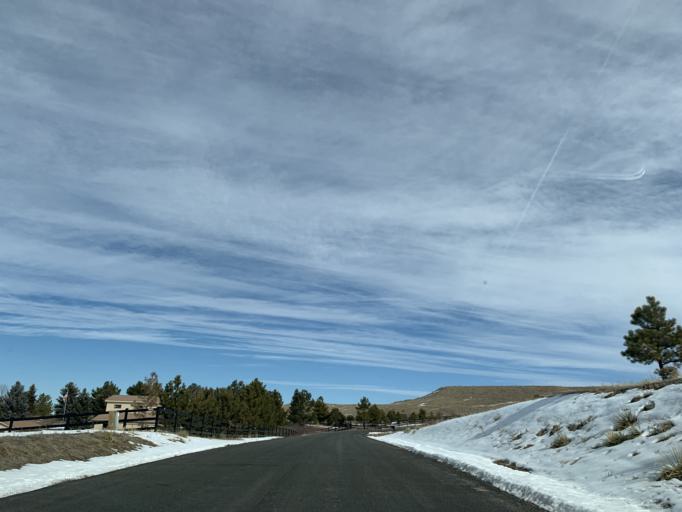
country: US
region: Colorado
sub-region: Douglas County
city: Carriage Club
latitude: 39.5180
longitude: -104.8990
